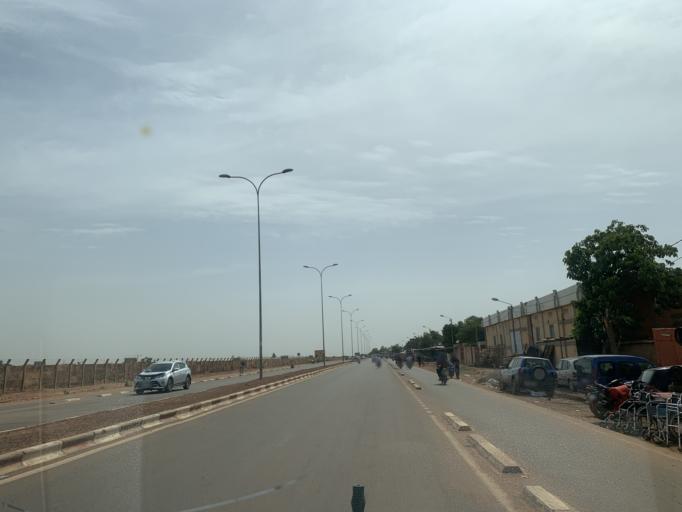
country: BF
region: Centre
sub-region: Kadiogo Province
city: Ouagadougou
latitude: 12.3363
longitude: -1.5198
